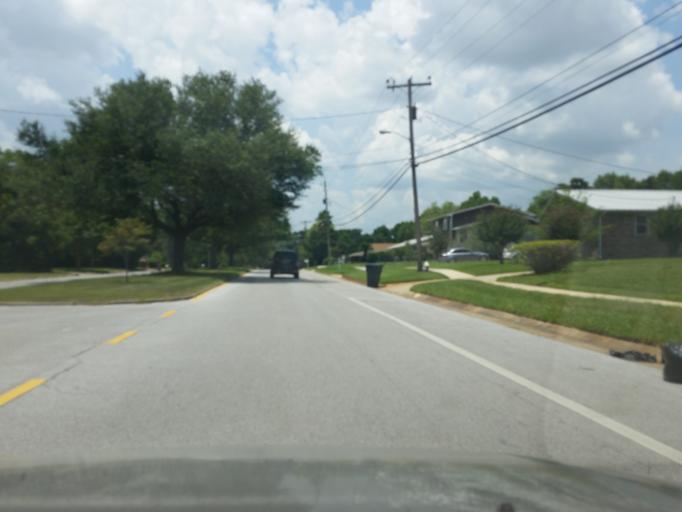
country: US
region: Florida
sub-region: Escambia County
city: East Pensacola Heights
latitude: 30.4573
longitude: -87.1714
